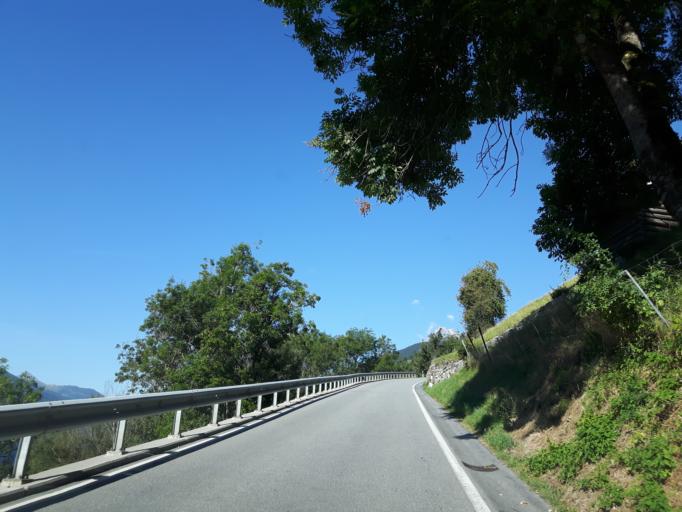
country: CH
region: Grisons
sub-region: Surselva District
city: Breil
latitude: 46.7769
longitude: 9.1309
